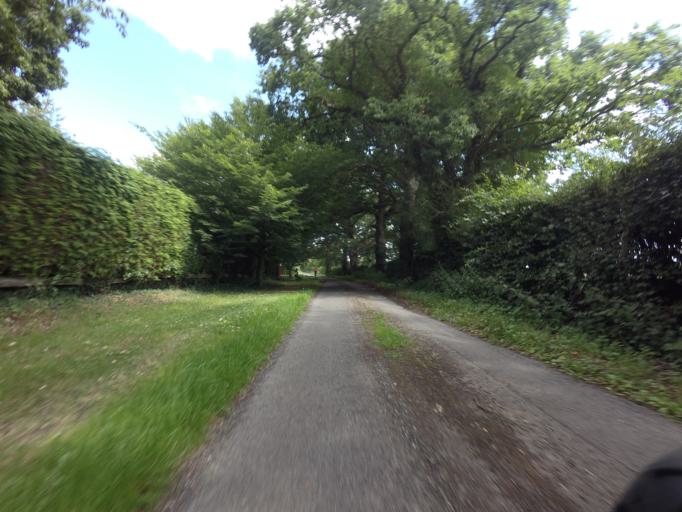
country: GB
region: England
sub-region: Kent
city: Tenterden
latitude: 51.0698
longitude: 0.7259
